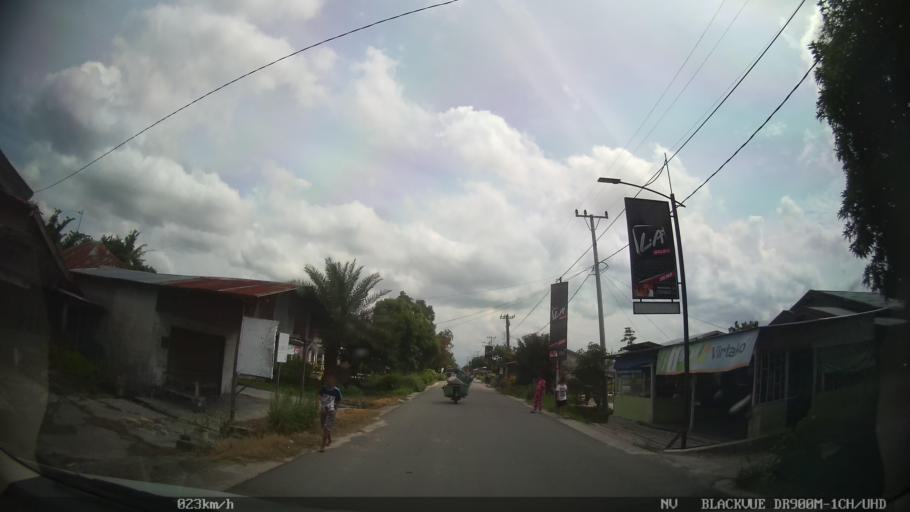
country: ID
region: North Sumatra
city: Percut
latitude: 3.5773
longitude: 98.8408
